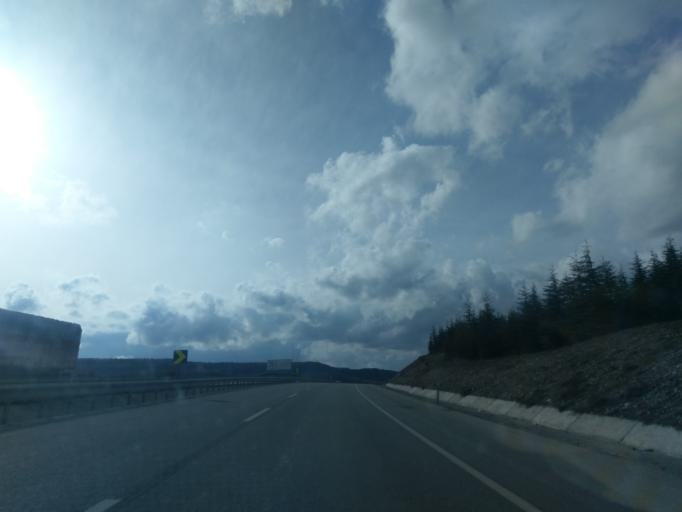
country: TR
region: Kuetahya
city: Sabuncu
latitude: 39.5710
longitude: 30.1127
